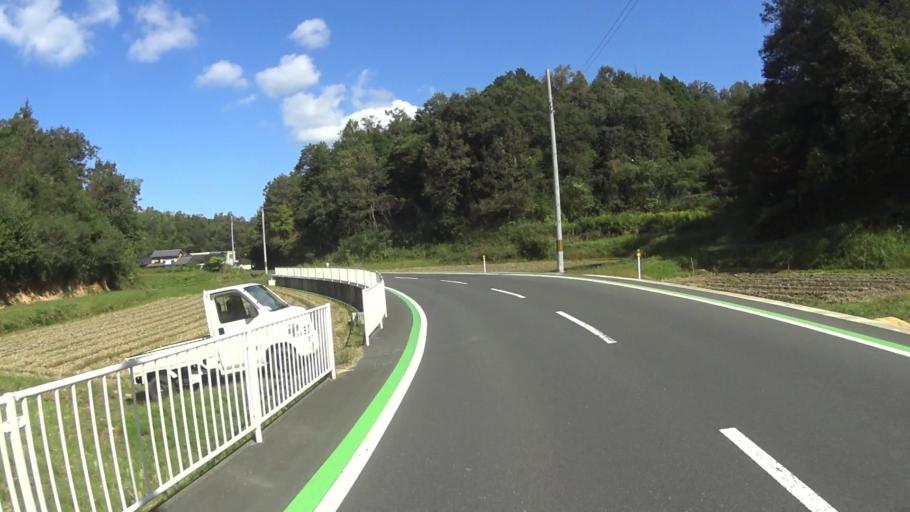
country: JP
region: Kyoto
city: Miyazu
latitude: 35.6370
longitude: 135.0704
